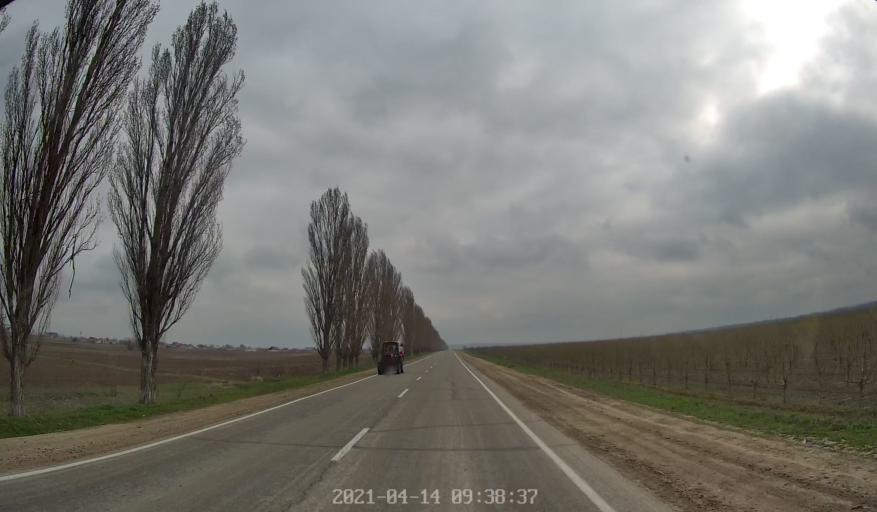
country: MD
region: Chisinau
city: Vadul lui Voda
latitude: 47.1258
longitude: 29.1191
